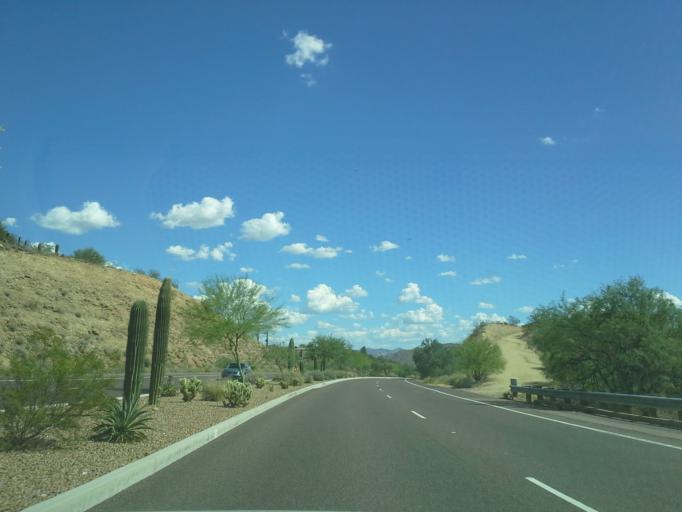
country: US
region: Arizona
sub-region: Maricopa County
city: Fountain Hills
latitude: 33.5815
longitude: -111.7331
